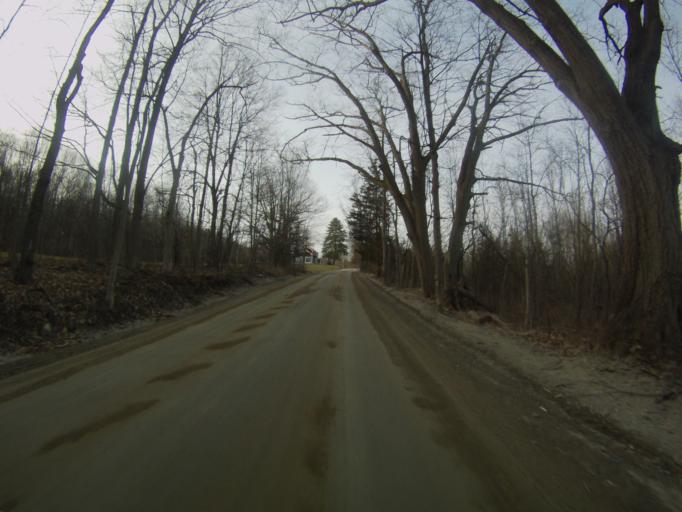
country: US
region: Vermont
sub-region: Addison County
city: Middlebury (village)
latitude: 44.0251
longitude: -73.2596
